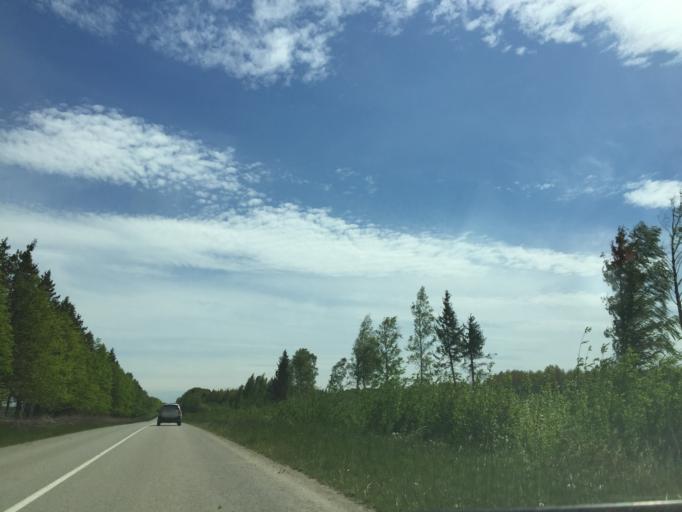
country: LT
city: Linkuva
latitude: 56.0420
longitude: 24.1292
